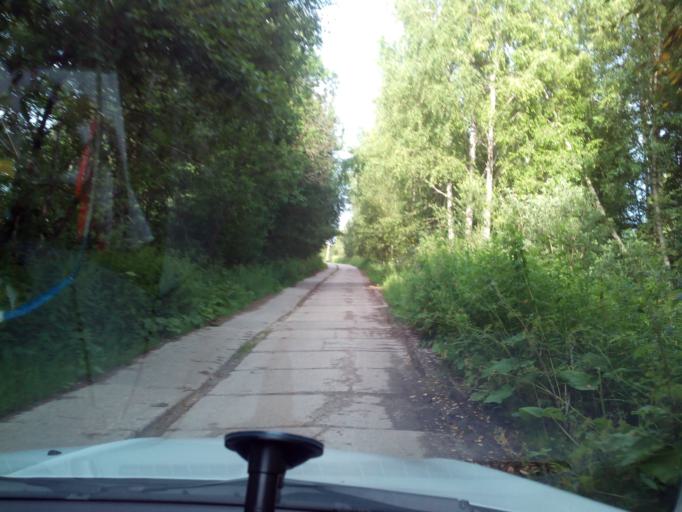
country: RU
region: Vladimir
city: Petushki
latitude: 56.0361
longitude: 39.5044
